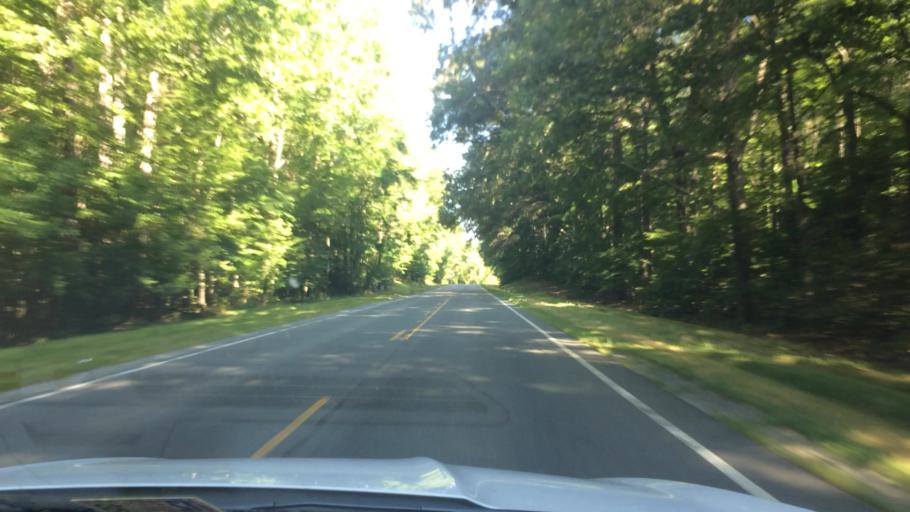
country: US
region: Virginia
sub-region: Lancaster County
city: Lancaster
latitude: 37.8125
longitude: -76.5451
